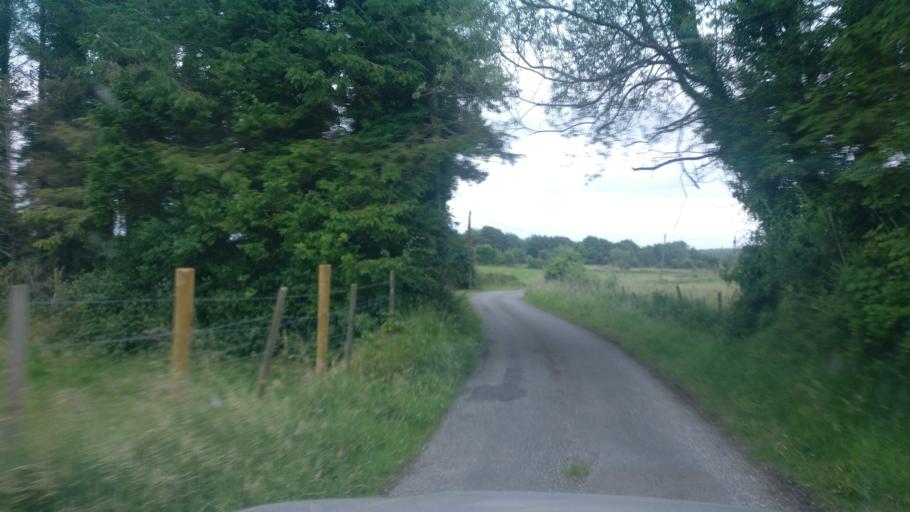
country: IE
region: Connaught
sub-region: County Galway
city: Ballinasloe
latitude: 53.3049
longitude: -8.3534
